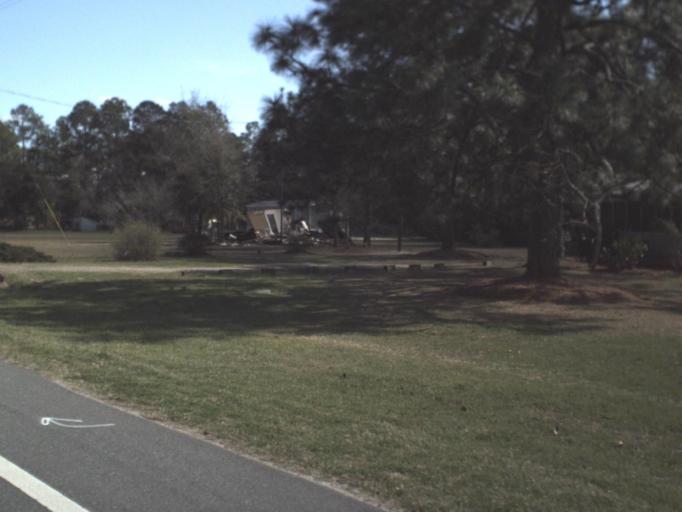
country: US
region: Florida
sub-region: Gadsden County
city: Gretna
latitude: 30.6914
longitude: -84.7321
